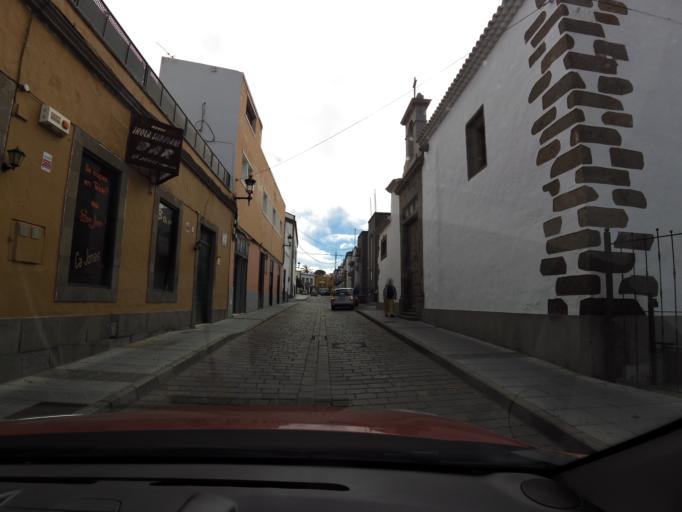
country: ES
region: Canary Islands
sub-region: Provincia de Las Palmas
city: Telde
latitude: 28.0043
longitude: -15.4146
